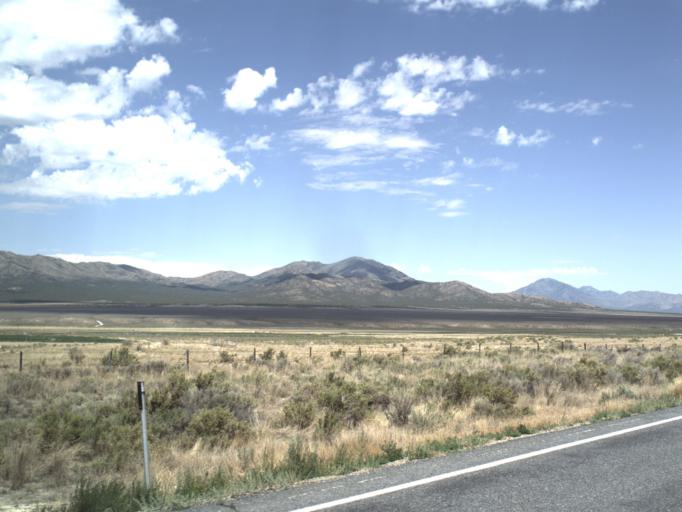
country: US
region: Utah
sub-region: Tooele County
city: Tooele
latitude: 40.1330
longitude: -112.4308
